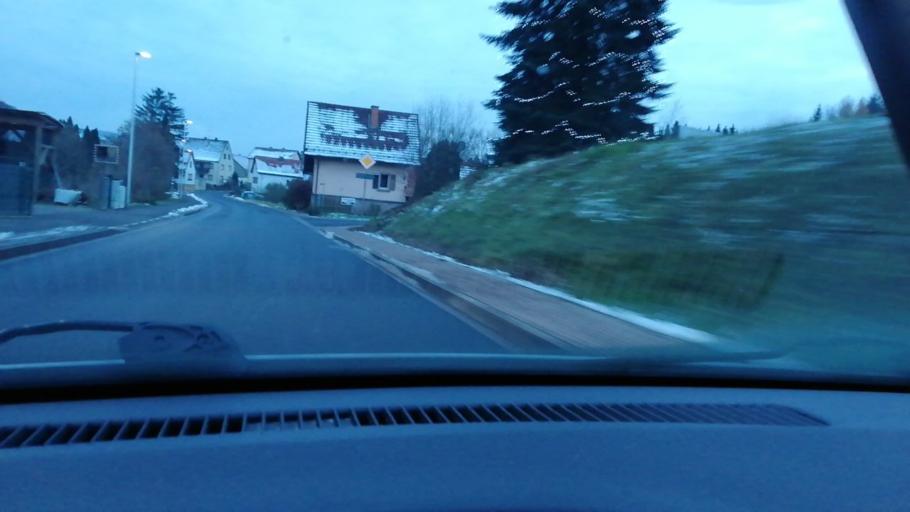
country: DE
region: Bavaria
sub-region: Regierungsbezirk Unterfranken
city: Krombach
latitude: 50.1011
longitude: 9.2271
